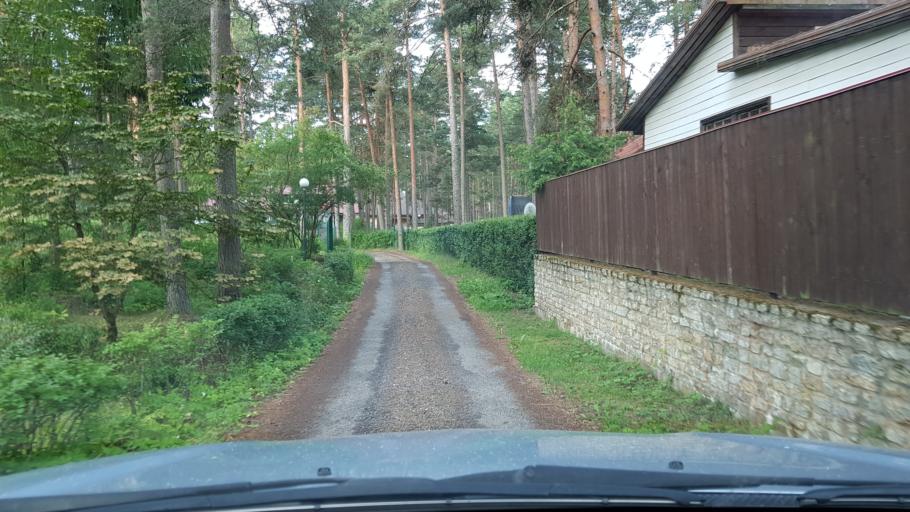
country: EE
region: Ida-Virumaa
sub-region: Narva-Joesuu linn
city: Narva-Joesuu
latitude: 59.4525
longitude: 28.0531
